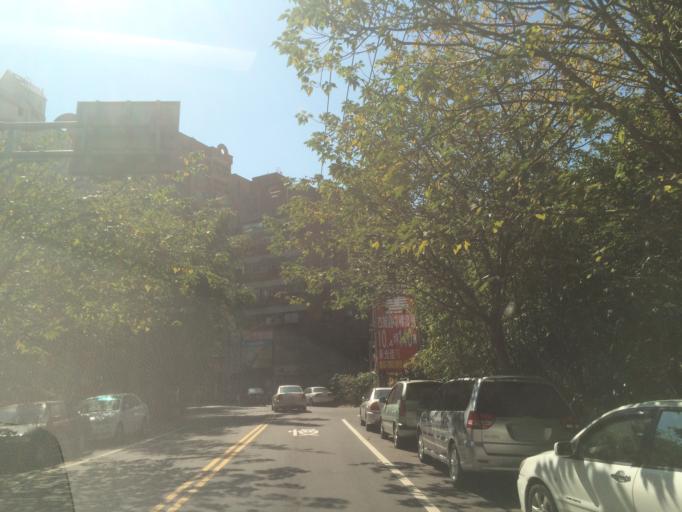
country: TW
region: Taiwan
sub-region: Hsinchu
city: Hsinchu
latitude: 24.7959
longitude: 120.9607
